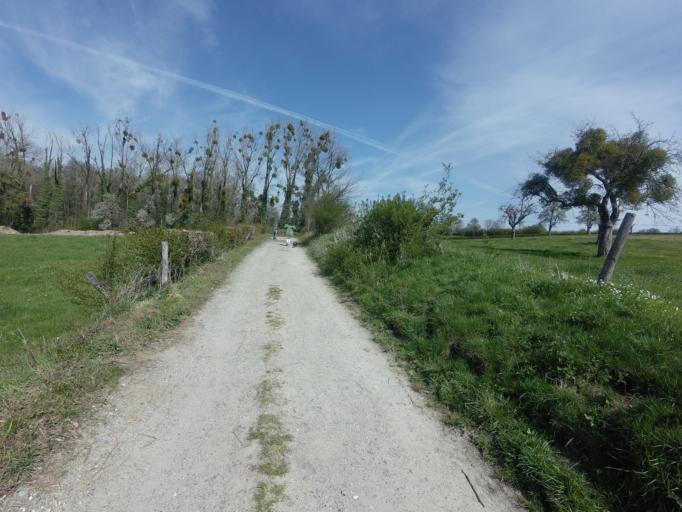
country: BE
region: Flanders
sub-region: Provincie Limburg
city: Sint-Pieters-Voeren
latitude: 50.7627
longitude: 5.7990
